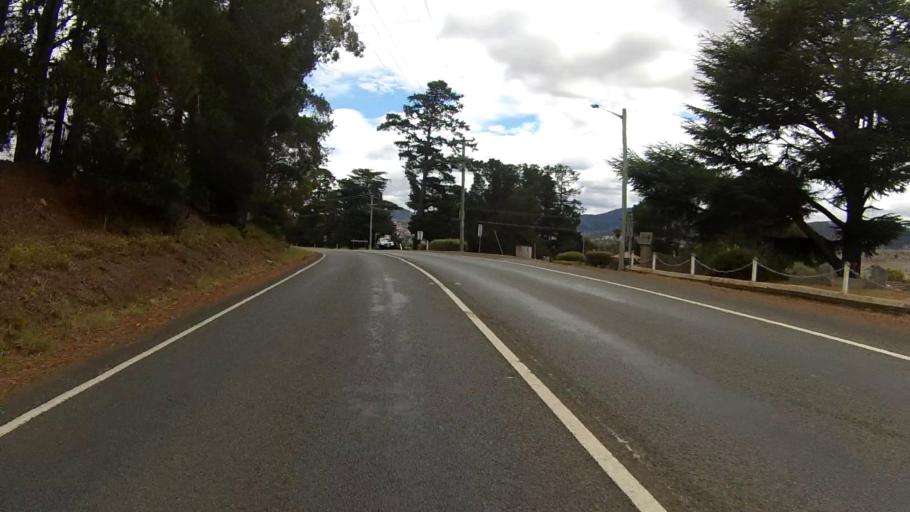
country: AU
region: Tasmania
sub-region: Brighton
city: Bridgewater
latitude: -42.6806
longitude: 147.2659
